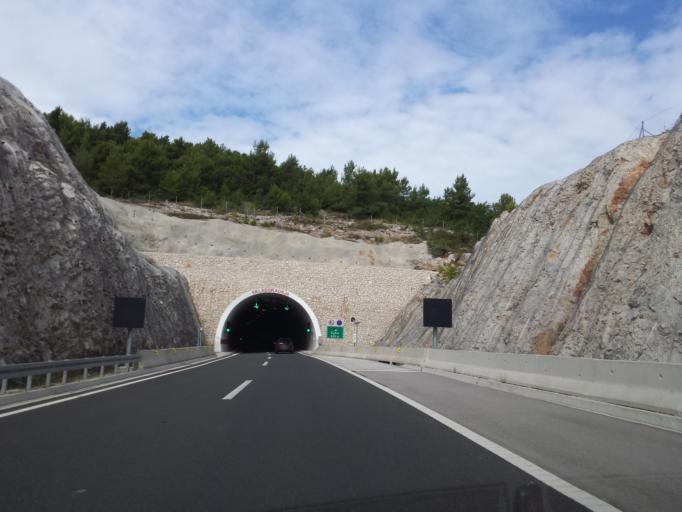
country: BA
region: Federation of Bosnia and Herzegovina
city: Vitina
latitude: 43.1614
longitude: 17.4729
